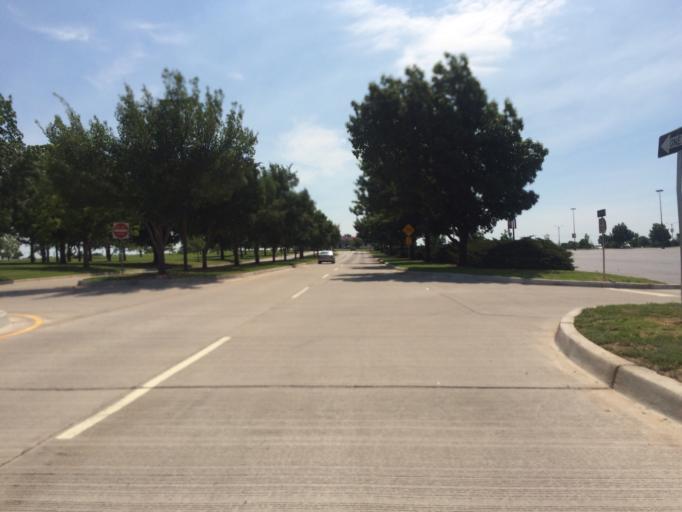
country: US
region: Oklahoma
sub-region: Cleveland County
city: Norman
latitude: 35.1894
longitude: -97.4443
